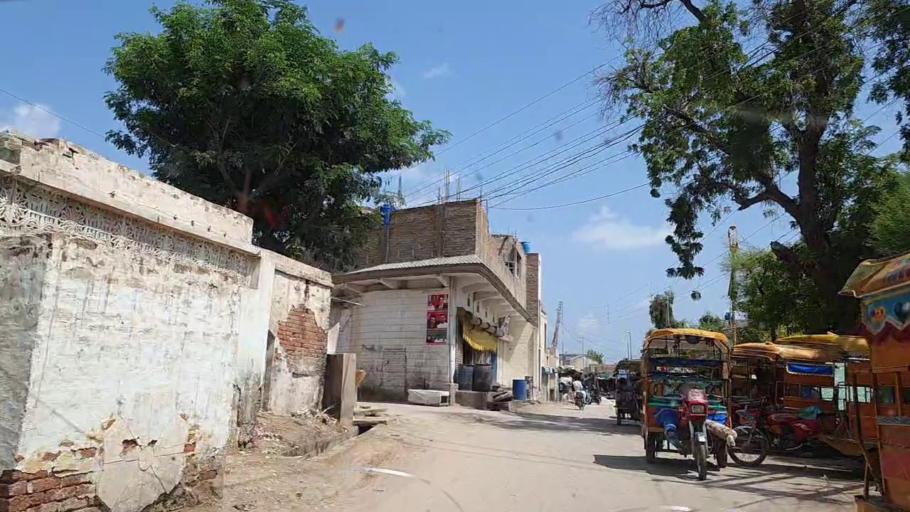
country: PK
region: Sindh
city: Tharu Shah
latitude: 26.9443
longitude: 68.1139
